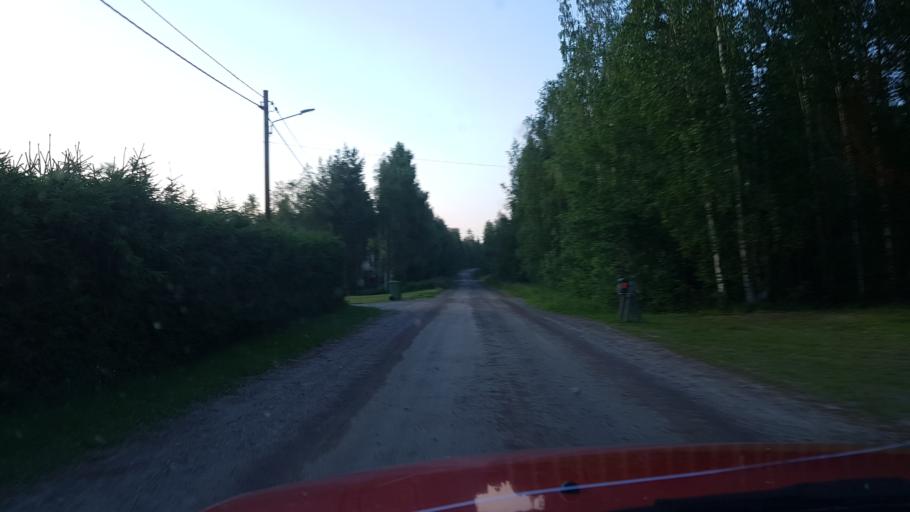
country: SE
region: Norrbotten
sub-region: Alvsbyns Kommun
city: AElvsbyn
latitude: 65.7013
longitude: 20.6809
